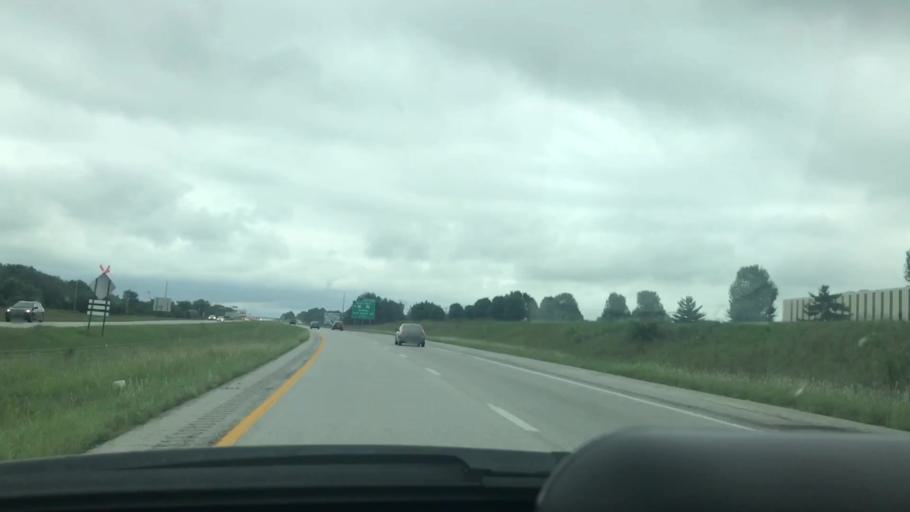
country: US
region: Missouri
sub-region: Jasper County
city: Duquesne
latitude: 37.0474
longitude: -94.4684
